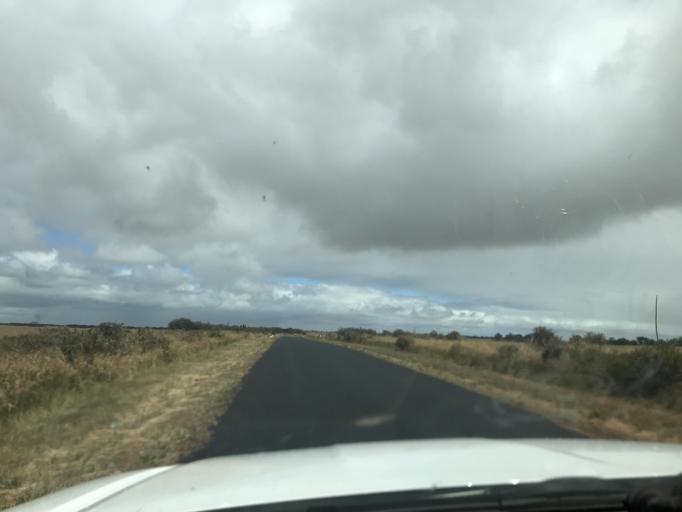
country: AU
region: South Australia
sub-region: Tatiara
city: Bordertown
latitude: -36.1350
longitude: 141.1810
